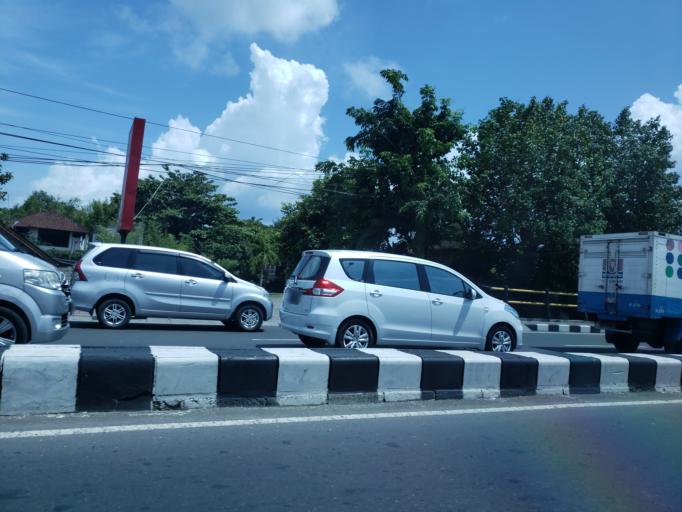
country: ID
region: Bali
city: Jabajero
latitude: -8.7282
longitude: 115.1797
